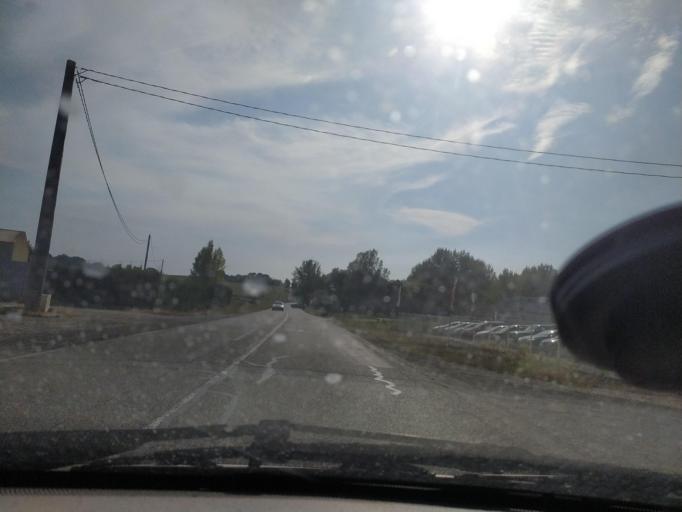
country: FR
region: Midi-Pyrenees
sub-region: Departement du Gers
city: Nogaro
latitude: 43.7955
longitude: 0.0329
